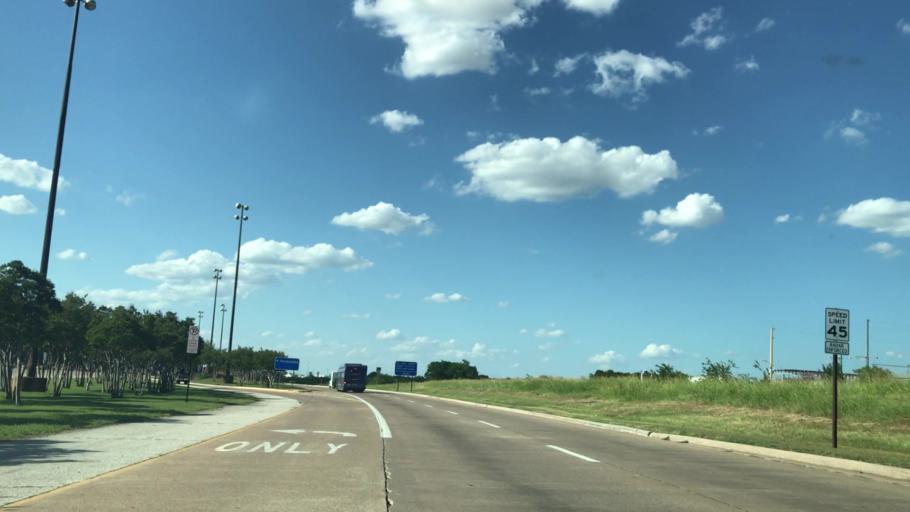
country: US
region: Texas
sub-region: Tarrant County
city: Euless
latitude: 32.8636
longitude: -97.0398
